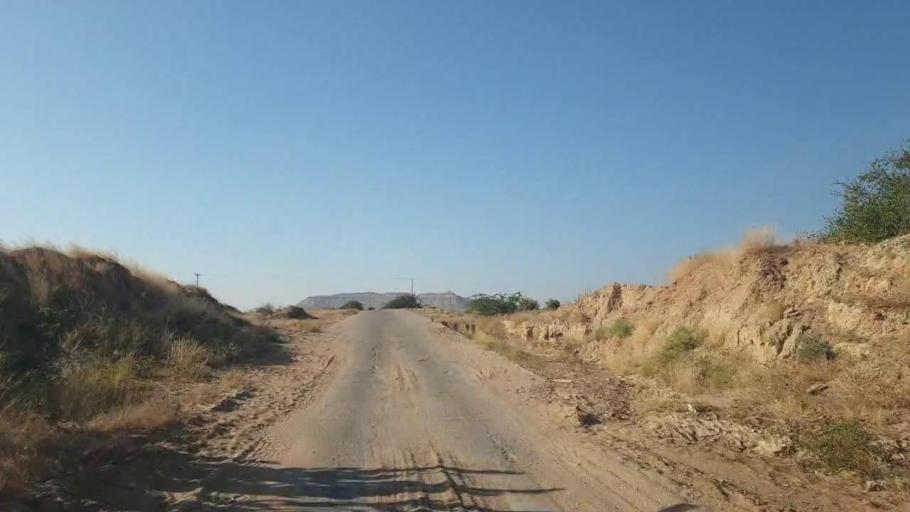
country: PK
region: Sindh
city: Malir Cantonment
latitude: 25.3878
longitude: 67.5273
